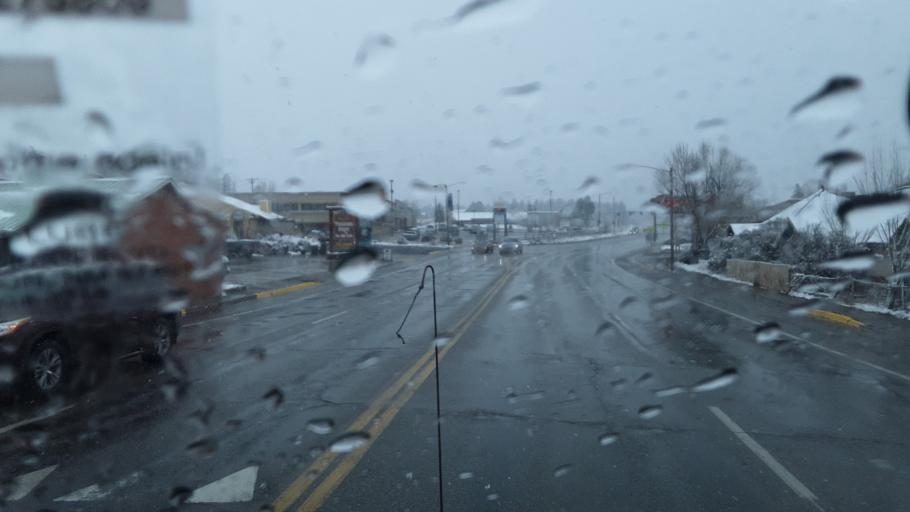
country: US
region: Colorado
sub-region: Archuleta County
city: Pagosa Springs
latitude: 37.2663
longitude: -107.0143
